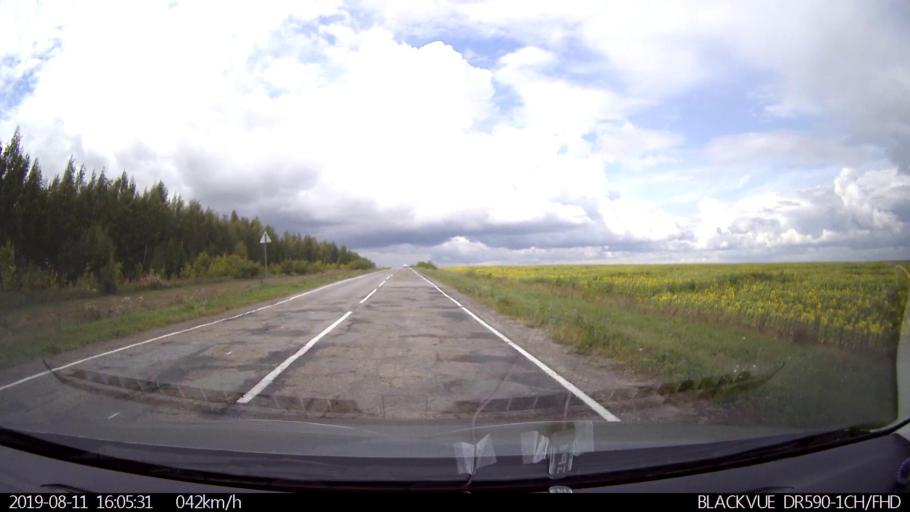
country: RU
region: Ulyanovsk
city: Ignatovka
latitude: 53.9613
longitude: 47.6490
